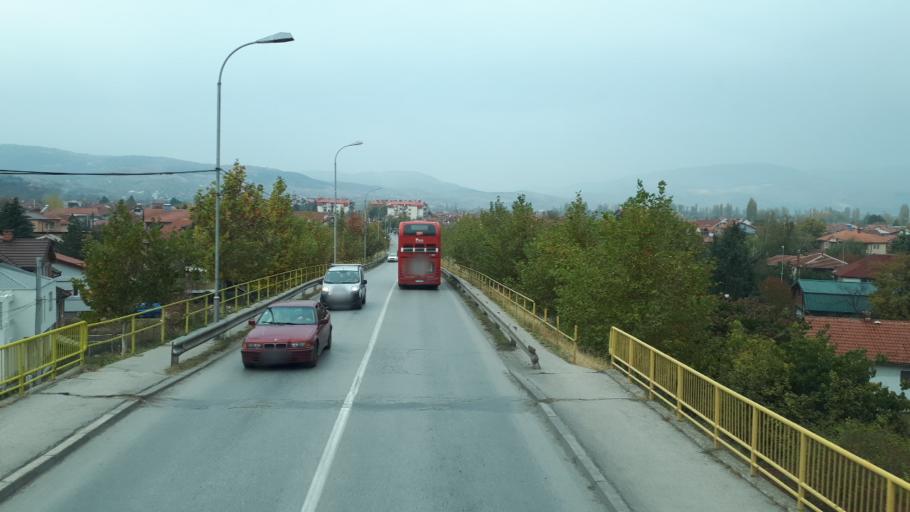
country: MK
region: Saraj
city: Saraj
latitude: 42.0132
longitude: 21.3594
